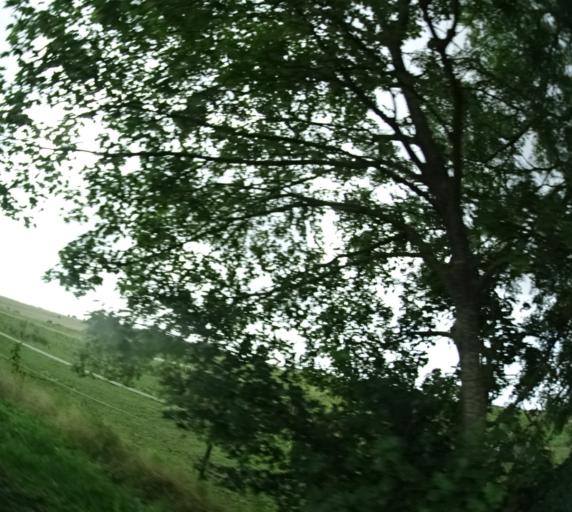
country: DK
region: Central Jutland
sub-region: Syddjurs Kommune
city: Ryomgard
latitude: 56.3879
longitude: 10.5591
